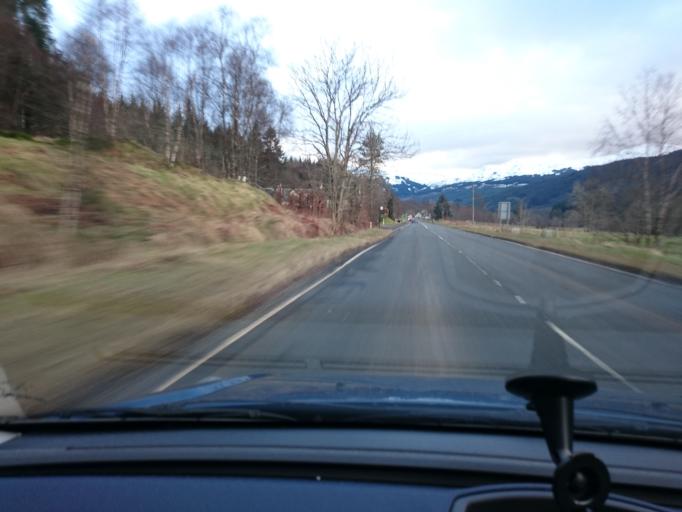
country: GB
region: Scotland
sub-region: Stirling
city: Callander
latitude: 56.3324
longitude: -4.3243
